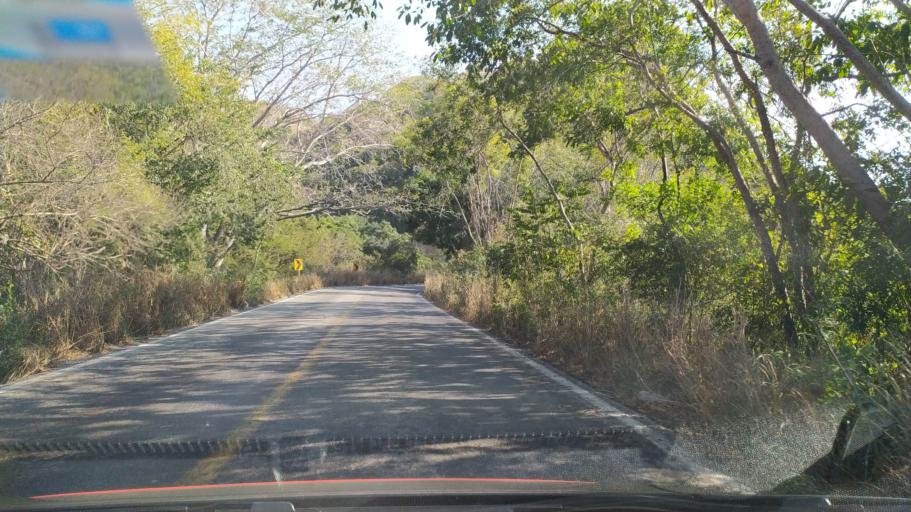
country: MX
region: Michoacan
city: Coahuayana Viejo
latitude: 18.6044
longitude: -103.6788
